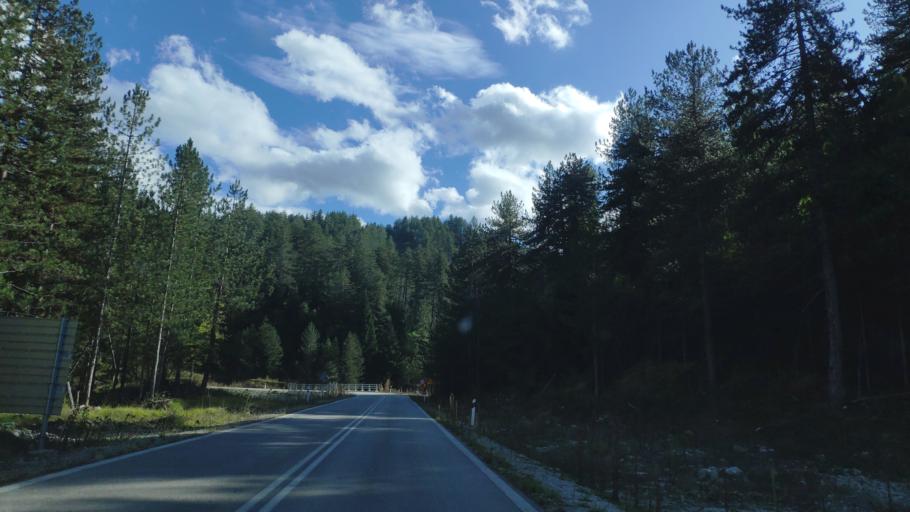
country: AL
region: Korce
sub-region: Rrethi i Devollit
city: Miras
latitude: 40.4104
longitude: 20.8740
